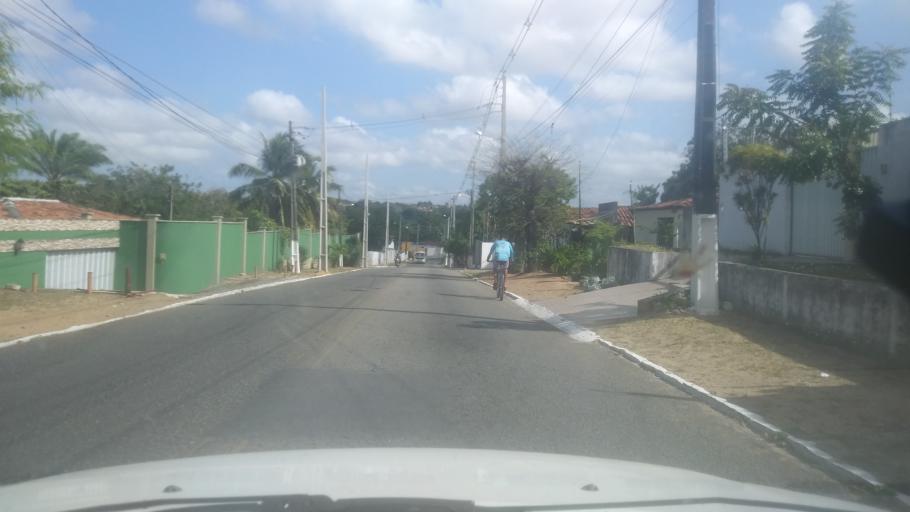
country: BR
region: Rio Grande do Norte
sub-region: Extremoz
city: Extremoz
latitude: -5.7078
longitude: -35.2799
